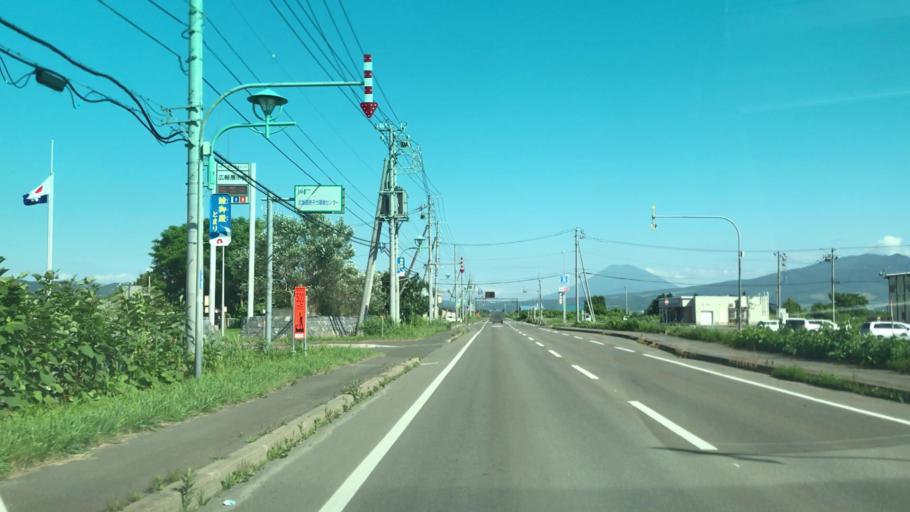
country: JP
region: Hokkaido
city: Iwanai
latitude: 43.0316
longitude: 140.5363
